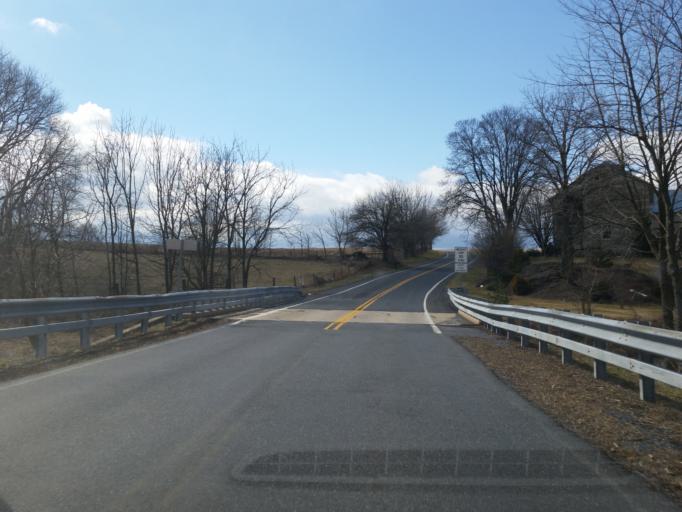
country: US
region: Pennsylvania
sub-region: Lebanon County
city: Palmyra
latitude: 40.3124
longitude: -76.5527
